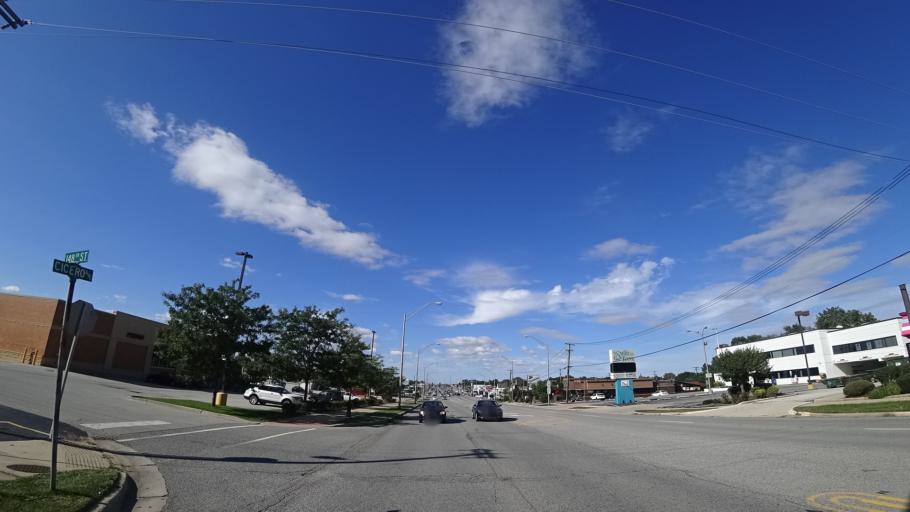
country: US
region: Illinois
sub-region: Cook County
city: Midlothian
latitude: 41.6233
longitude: -87.7373
